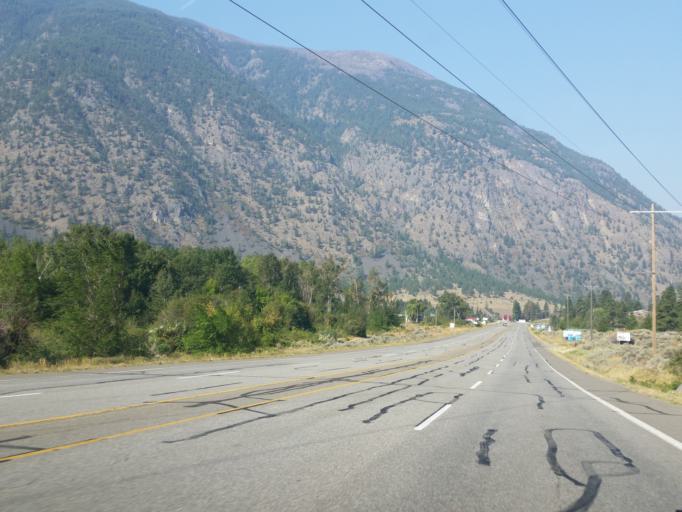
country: CA
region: British Columbia
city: Oliver
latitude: 49.2054
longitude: -119.8740
